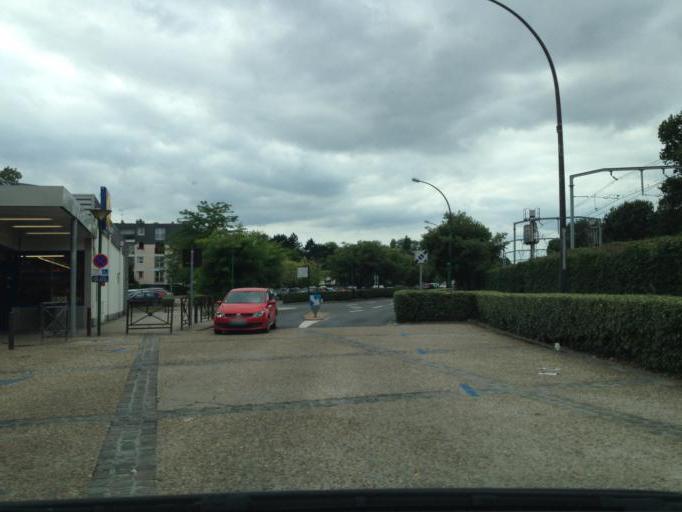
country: FR
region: Ile-de-France
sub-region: Departement de l'Essonne
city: Gif-sur-Yvette
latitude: 48.6973
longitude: 2.1299
